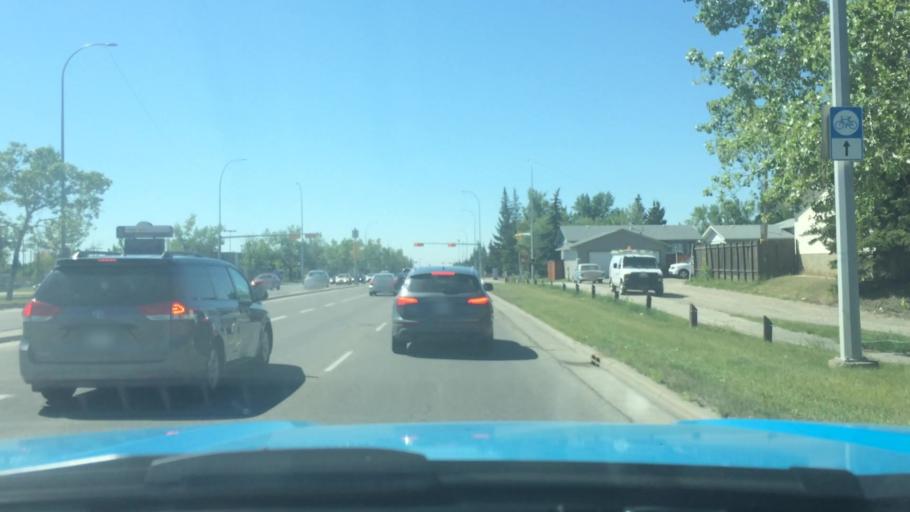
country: CA
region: Alberta
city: Calgary
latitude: 51.0773
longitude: -113.9585
